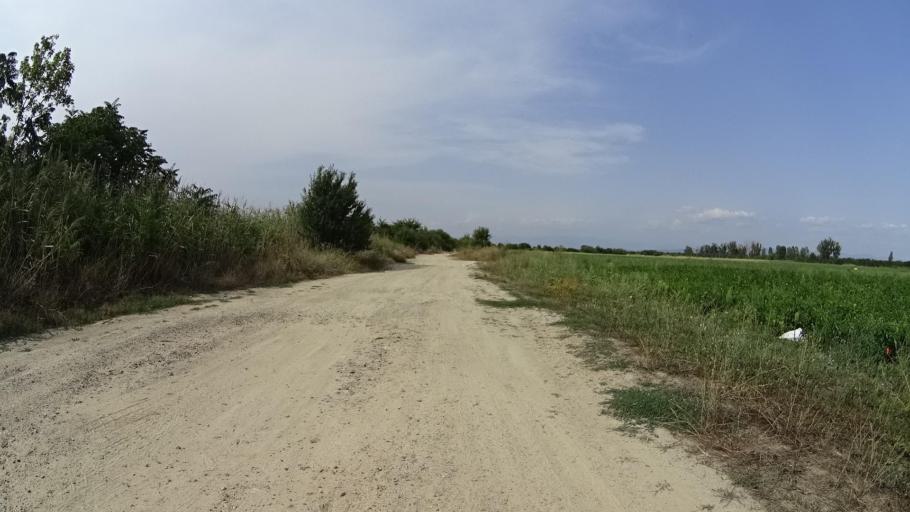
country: BG
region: Plovdiv
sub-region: Obshtina Kaloyanovo
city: Kaloyanovo
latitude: 42.2938
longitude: 24.7960
